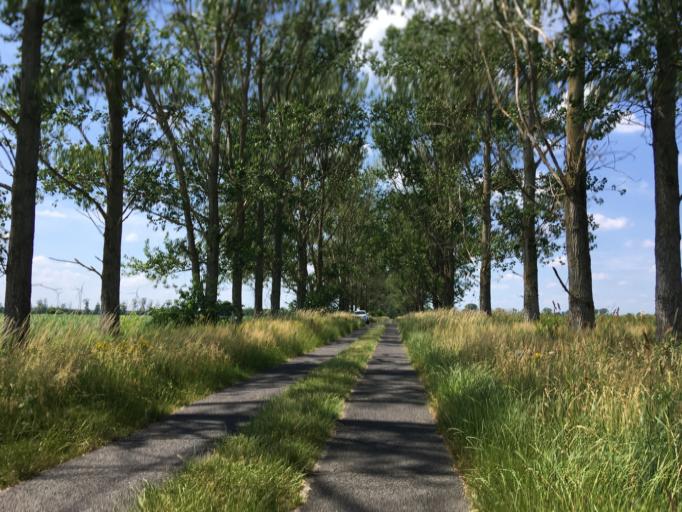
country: DE
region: Brandenburg
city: Werneuchen
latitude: 52.6931
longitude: 13.7345
